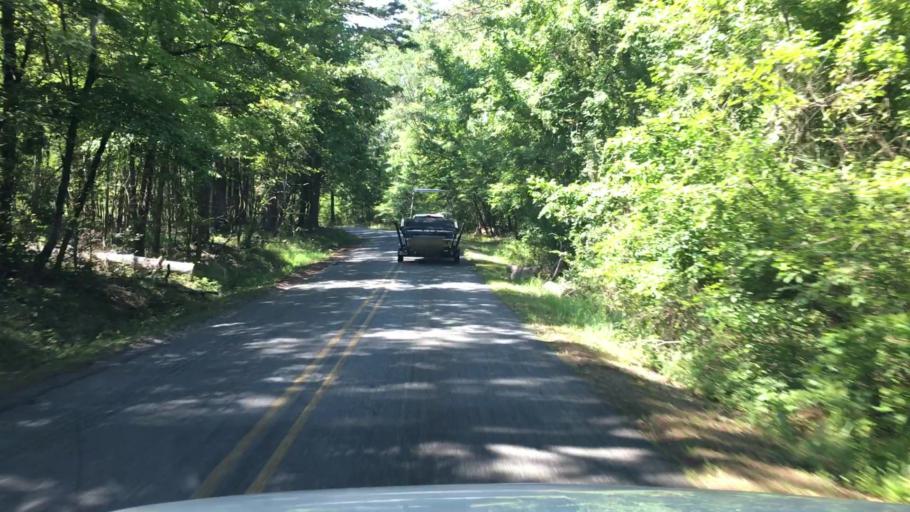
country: US
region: Arkansas
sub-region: Garland County
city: Piney
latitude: 34.5382
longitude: -93.3416
